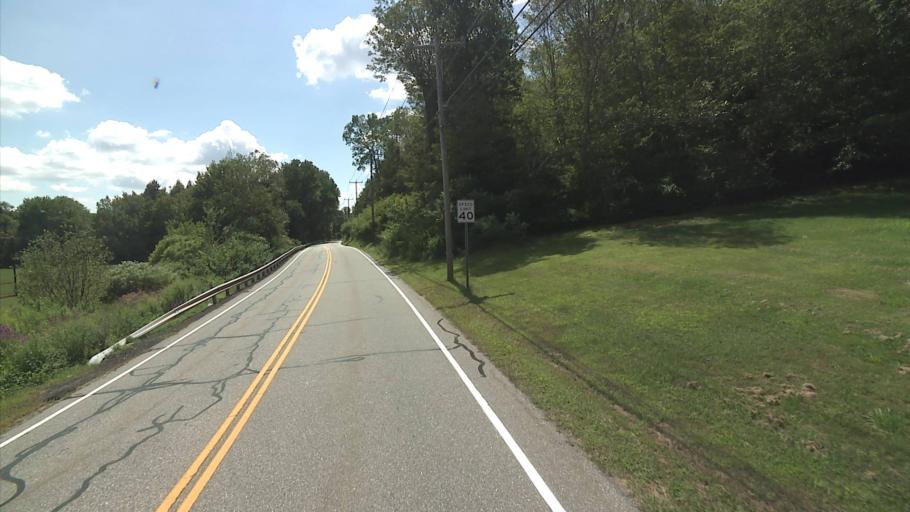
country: US
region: Connecticut
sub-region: Windham County
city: South Woodstock
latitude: 41.8988
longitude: -72.0798
